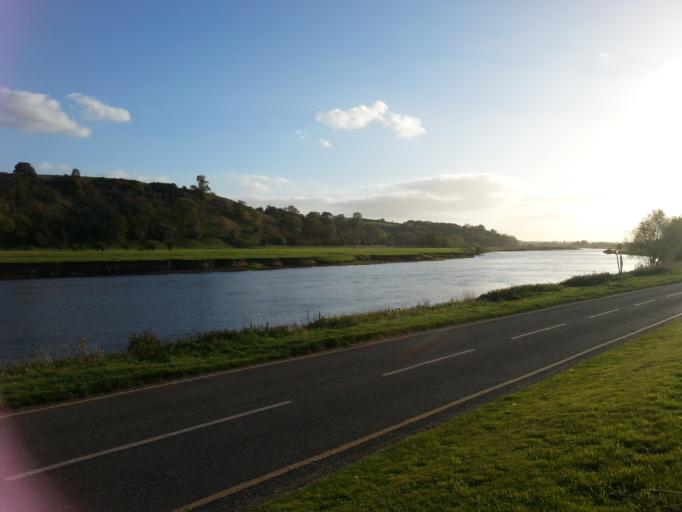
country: GB
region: England
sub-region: Nottinghamshire
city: East Bridgford
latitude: 53.0095
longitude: -0.9535
